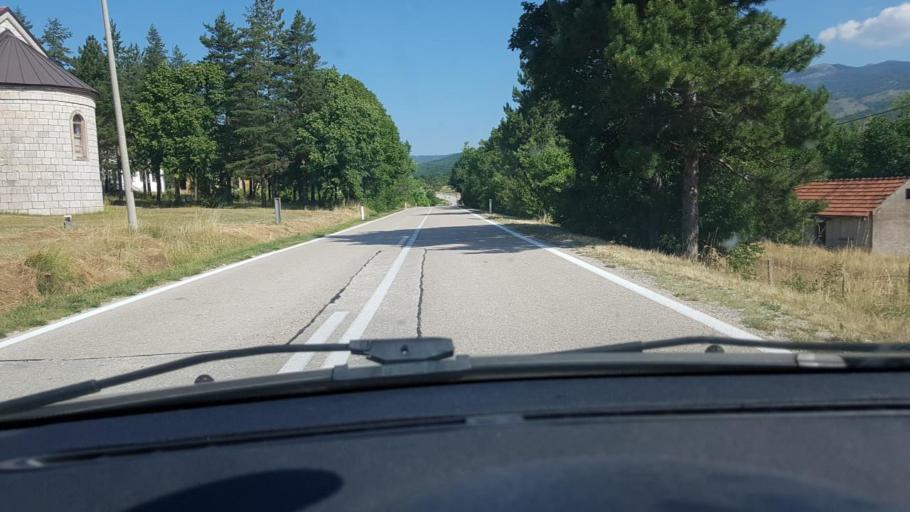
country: BA
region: Federation of Bosnia and Herzegovina
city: Bosansko Grahovo
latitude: 44.0834
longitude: 16.5695
